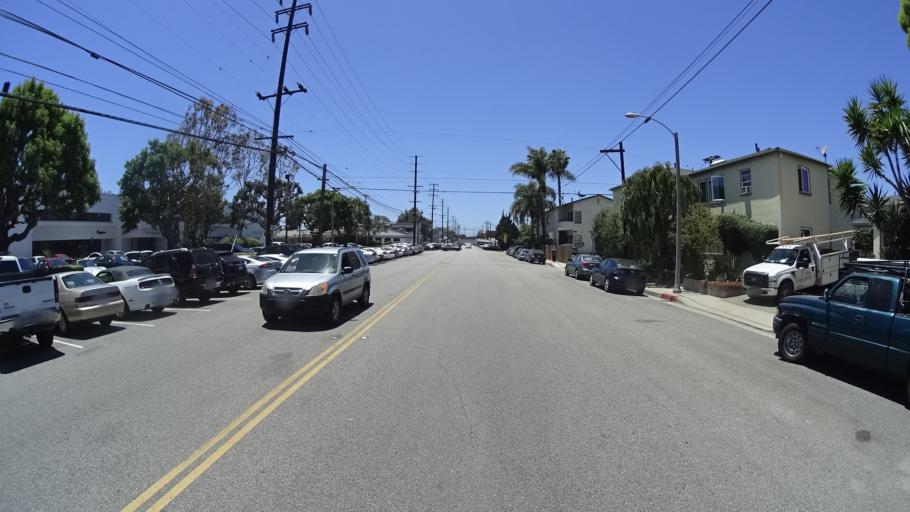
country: US
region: California
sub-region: Los Angeles County
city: Santa Monica
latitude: 34.0331
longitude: -118.4617
